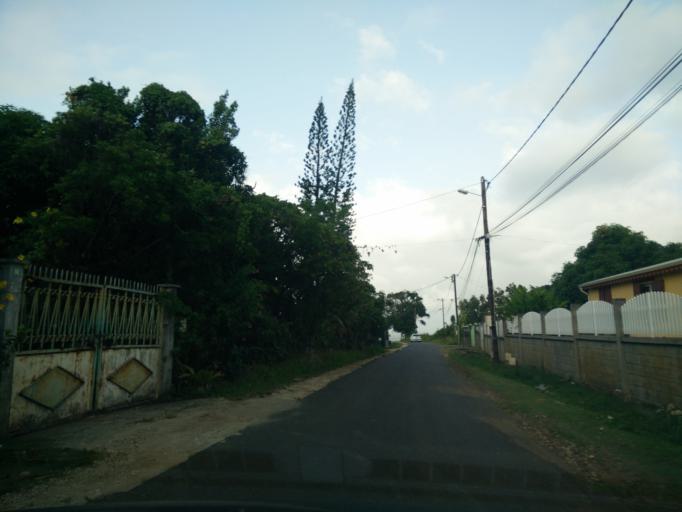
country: GP
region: Guadeloupe
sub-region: Guadeloupe
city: Petit-Bourg
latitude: 16.1851
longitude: -61.6148
